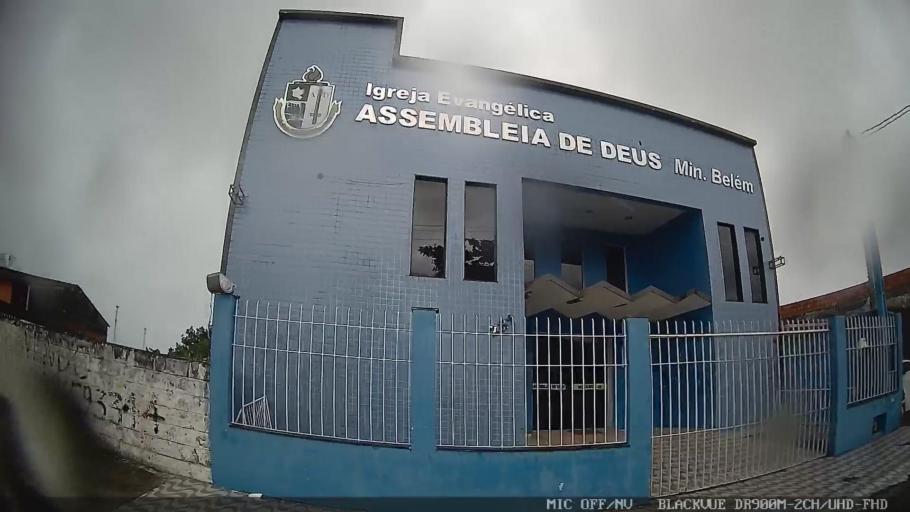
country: BR
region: Sao Paulo
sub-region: Itanhaem
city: Itanhaem
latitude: -24.1890
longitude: -46.8188
